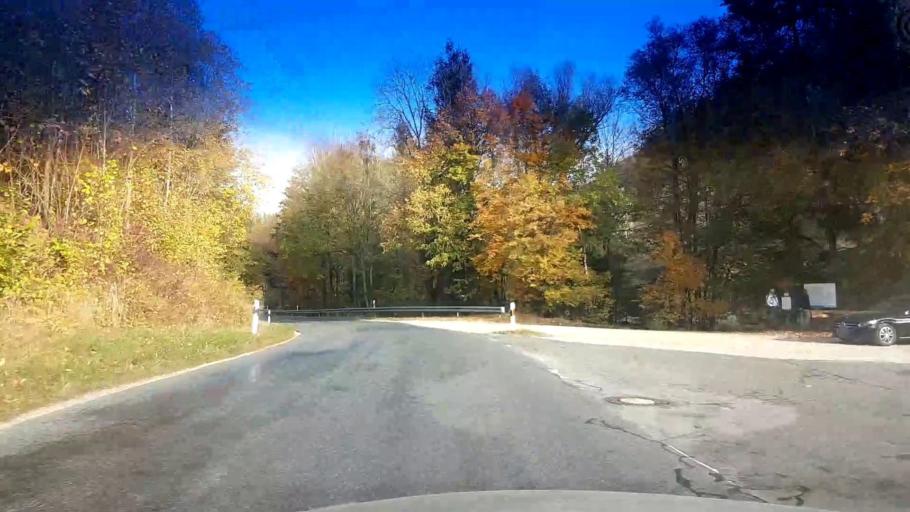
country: DE
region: Bavaria
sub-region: Upper Franconia
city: Stadelhofen
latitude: 50.0228
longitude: 11.1985
